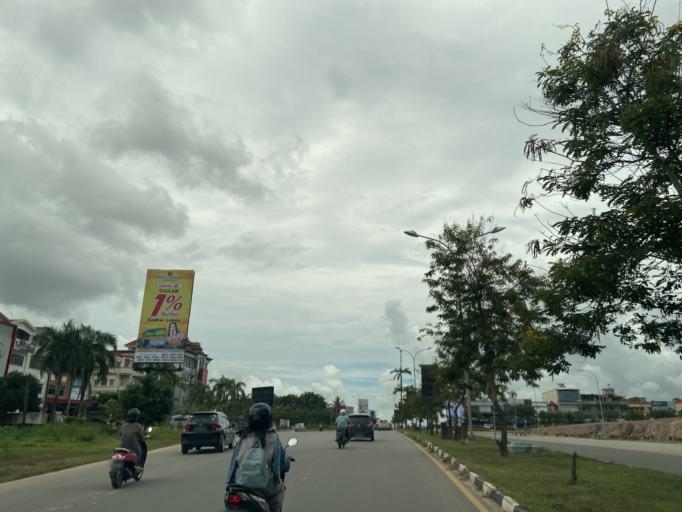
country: SG
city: Singapore
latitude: 1.1281
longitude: 104.0308
